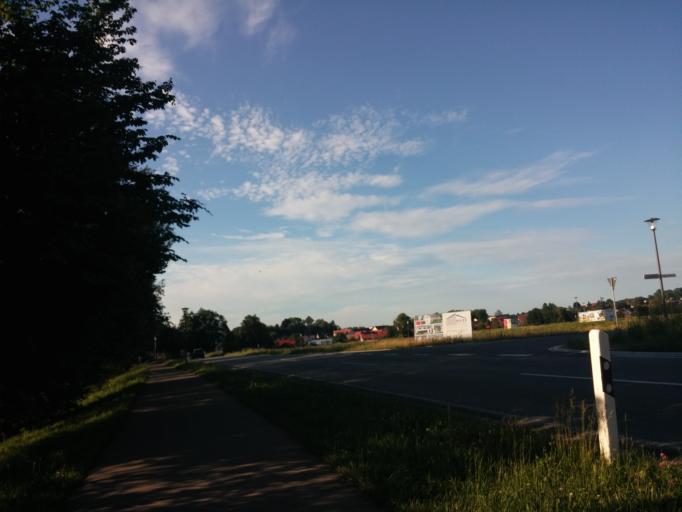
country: DE
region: Baden-Wuerttemberg
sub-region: Tuebingen Region
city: Kisslegg
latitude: 47.7829
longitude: 9.8806
